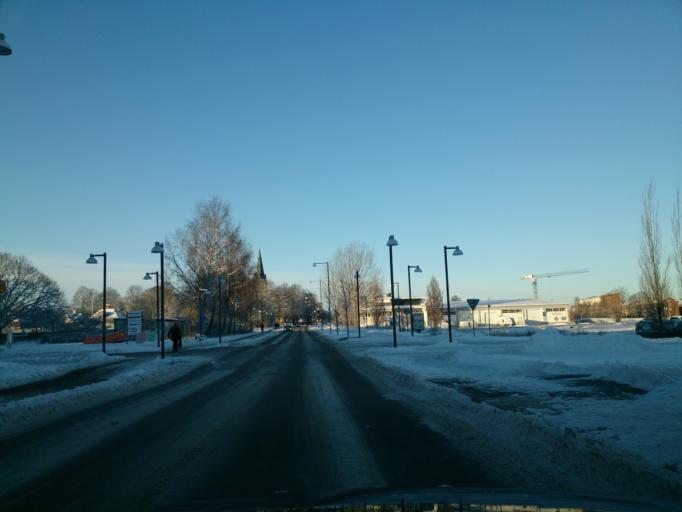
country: SE
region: OEstergoetland
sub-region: Norrkopings Kommun
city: Norrkoping
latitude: 58.5746
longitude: 16.2025
